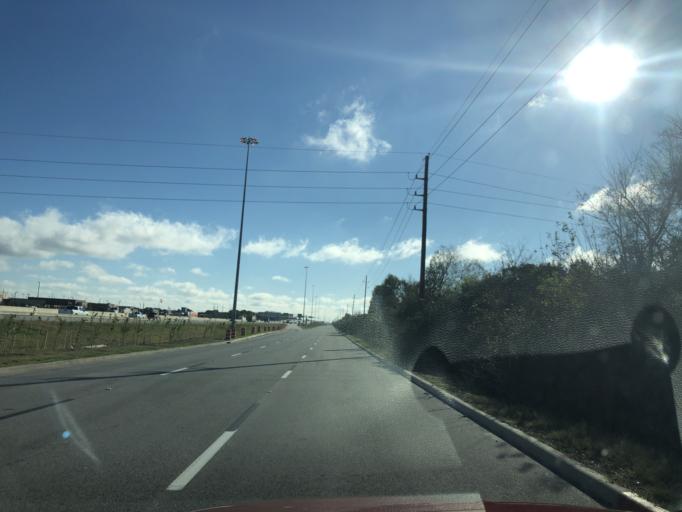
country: US
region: Texas
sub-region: Harris County
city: Cypress
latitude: 29.9924
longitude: -95.7539
